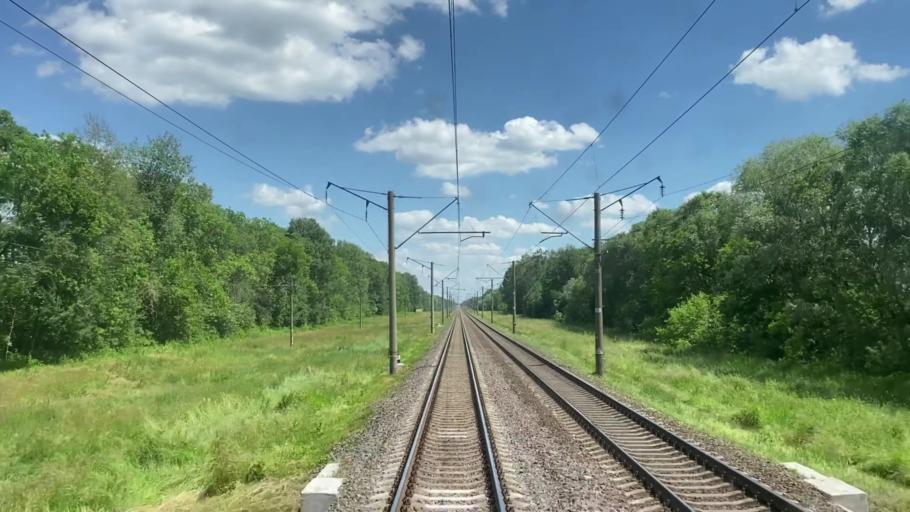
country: BY
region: Brest
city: Pruzhany
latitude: 52.5033
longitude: 24.6359
